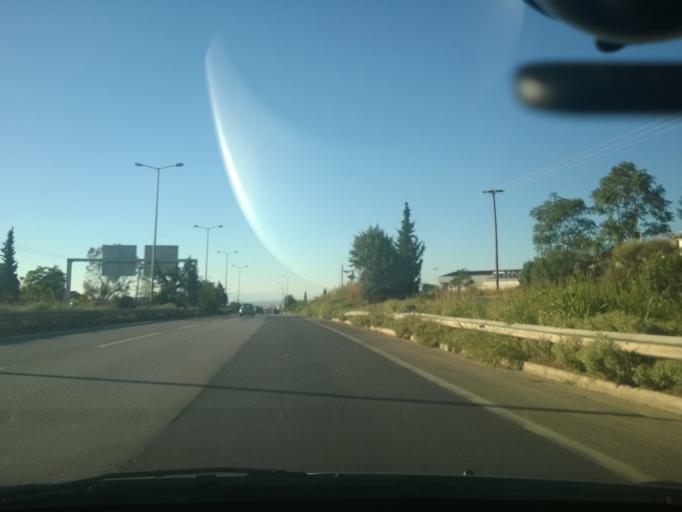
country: GR
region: Central Macedonia
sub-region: Nomos Thessalonikis
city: Pylaia
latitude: 40.5858
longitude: 22.9727
